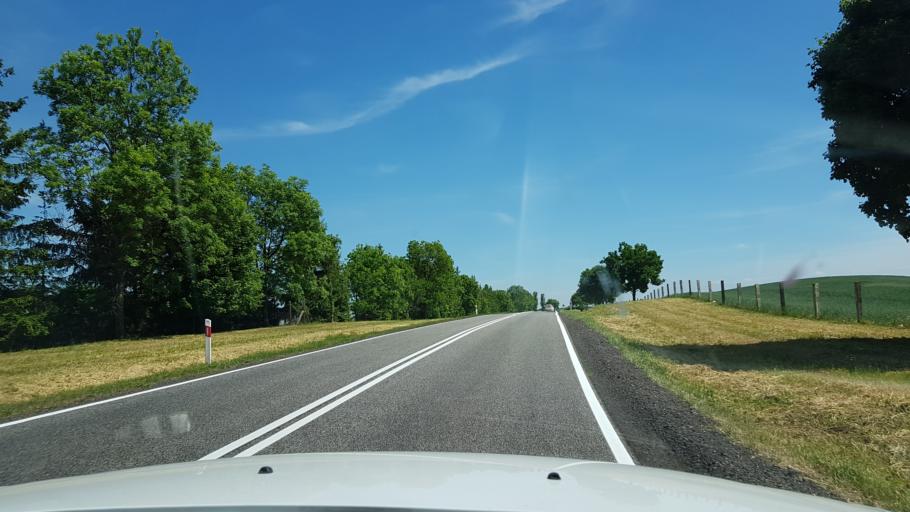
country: PL
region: West Pomeranian Voivodeship
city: Trzcinsko Zdroj
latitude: 52.9604
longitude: 14.5229
